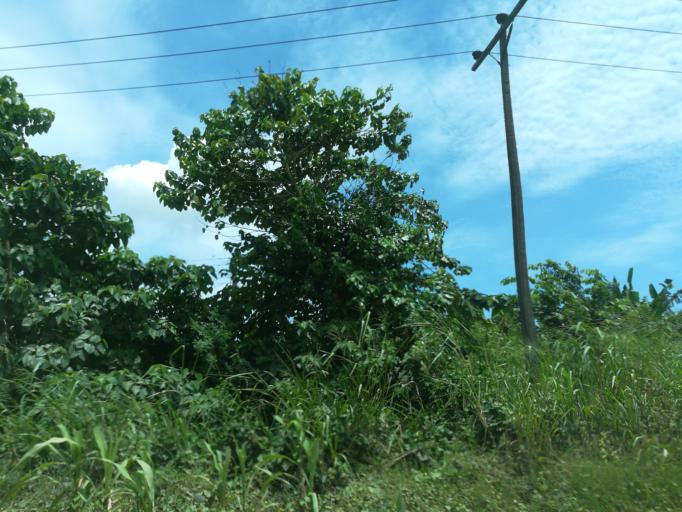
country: NG
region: Lagos
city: Ebute Ikorodu
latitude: 6.5948
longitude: 3.4934
